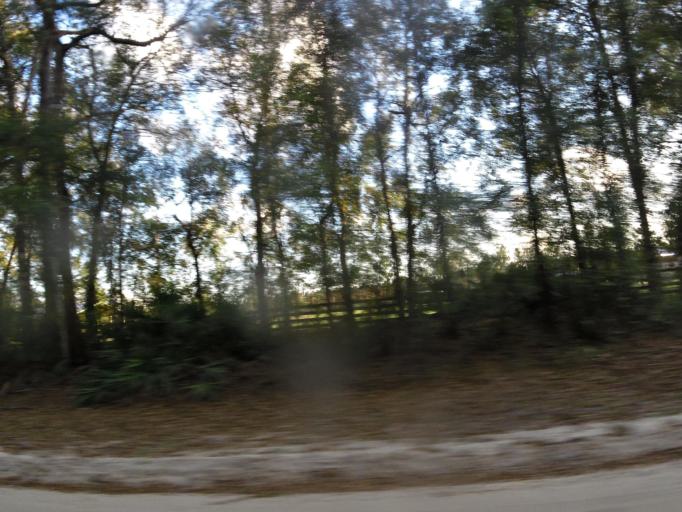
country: US
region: Florida
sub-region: Putnam County
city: Interlachen
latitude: 29.7794
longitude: -81.8488
